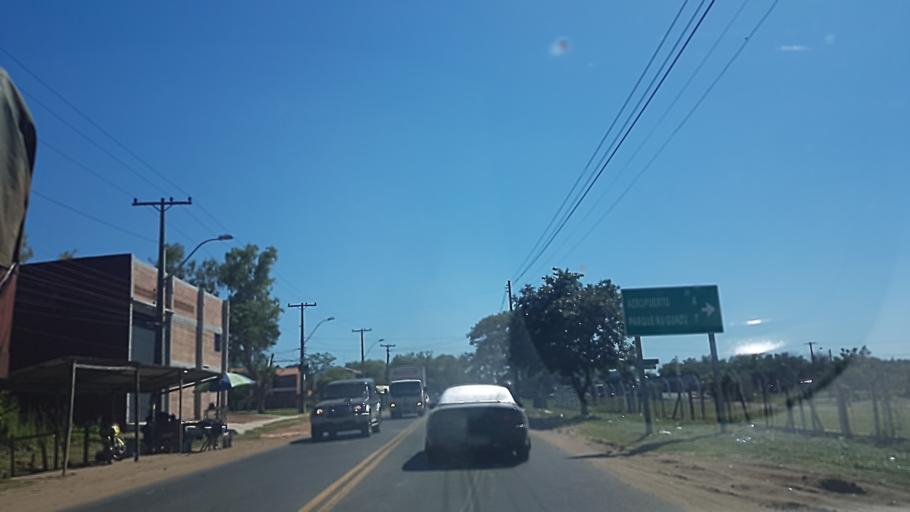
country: PY
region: Central
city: Limpio
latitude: -25.2115
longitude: -57.5124
